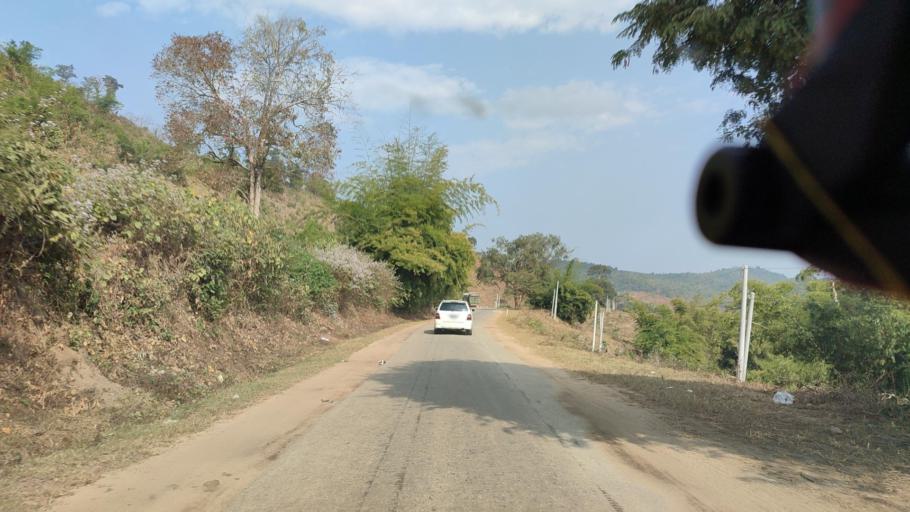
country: CN
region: Yunnan
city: Nayun
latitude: 21.8092
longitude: 99.5684
